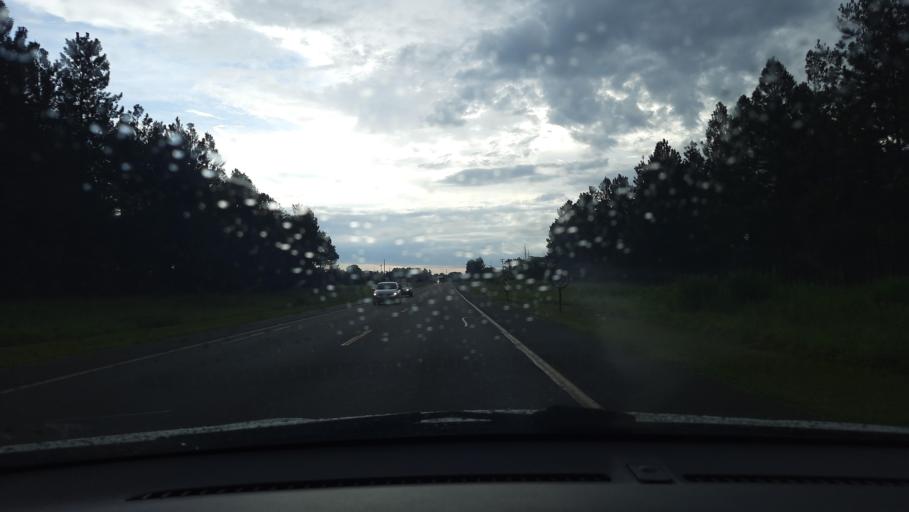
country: BR
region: Sao Paulo
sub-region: Casa Branca
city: Casa Branca
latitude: -21.7710
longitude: -47.0514
